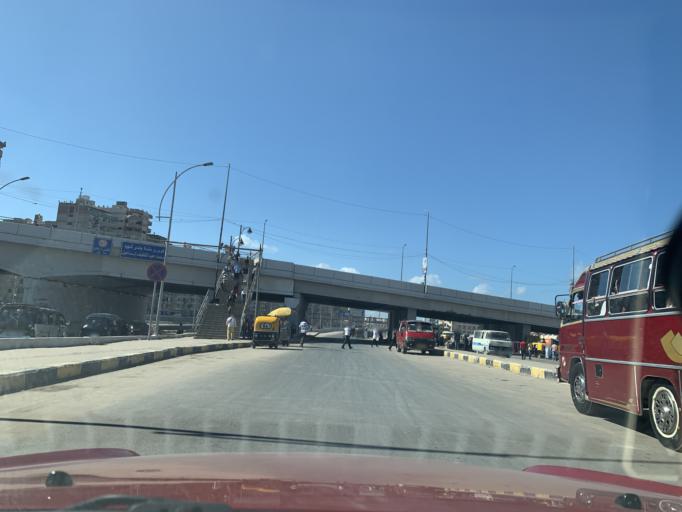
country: EG
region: Alexandria
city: Alexandria
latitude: 31.2188
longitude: 29.9947
